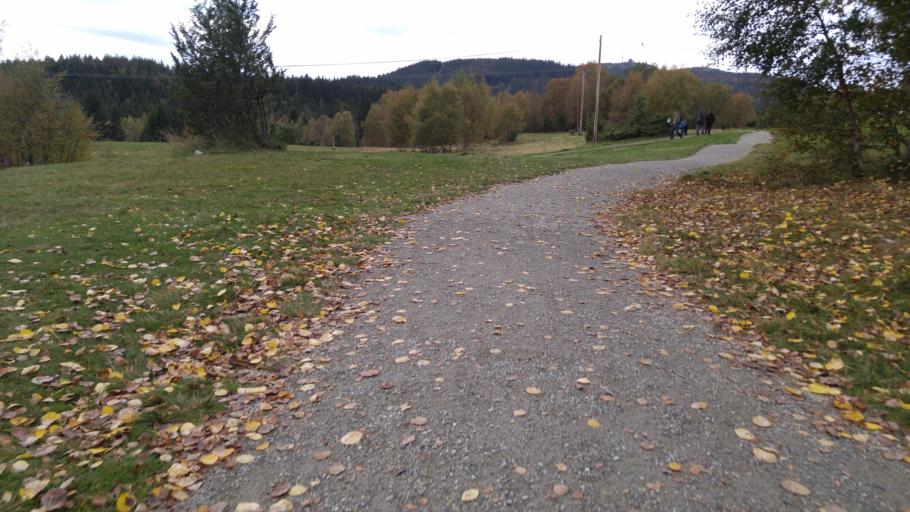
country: NO
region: Sor-Trondelag
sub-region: Trondheim
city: Trondheim
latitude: 63.4225
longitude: 10.3059
